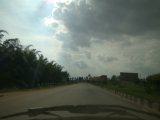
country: IN
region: Karnataka
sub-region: Bangalore Rural
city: Dasarahalli
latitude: 13.1341
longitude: 77.9407
